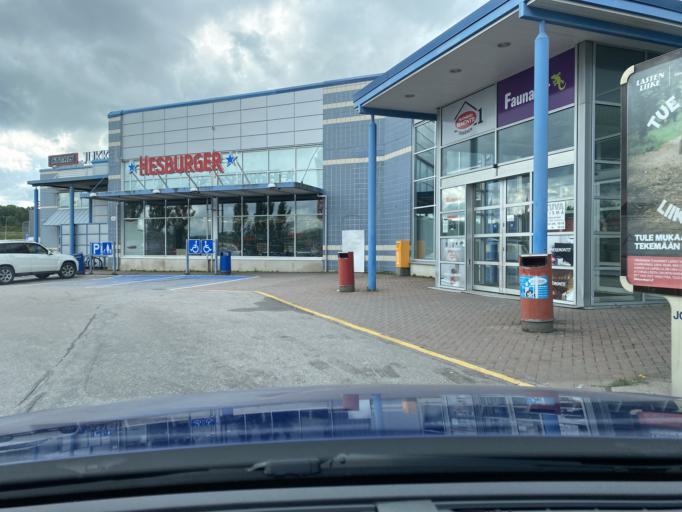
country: FI
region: Pirkanmaa
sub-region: Tampere
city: Tampere
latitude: 61.4654
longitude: 23.7228
